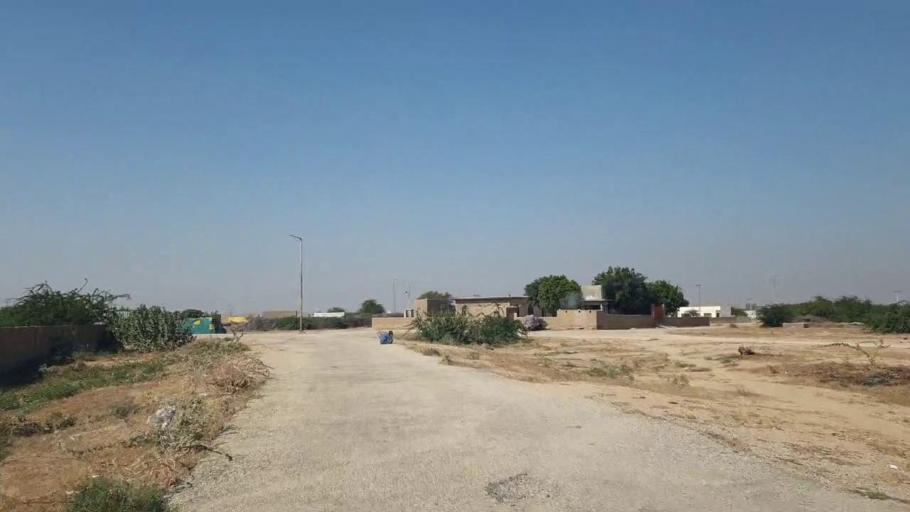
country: PK
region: Sindh
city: Jamshoro
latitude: 25.3518
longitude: 67.8316
